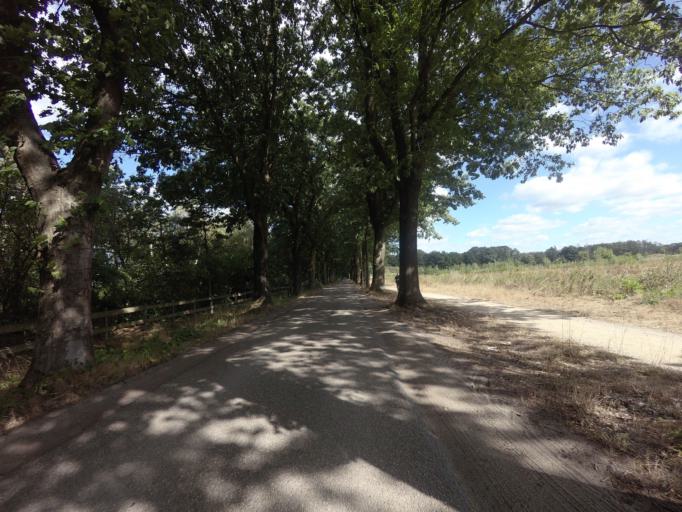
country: NL
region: North Brabant
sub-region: Gemeente Landerd
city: Schaijk
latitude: 51.7277
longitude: 5.6312
